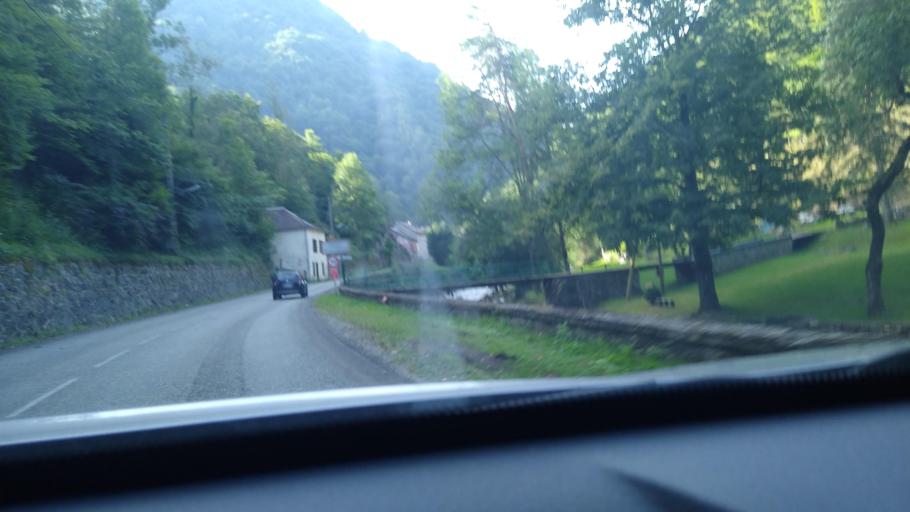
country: FR
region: Midi-Pyrenees
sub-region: Departement de l'Ariege
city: Saint-Girons
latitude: 42.8340
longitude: 1.1978
